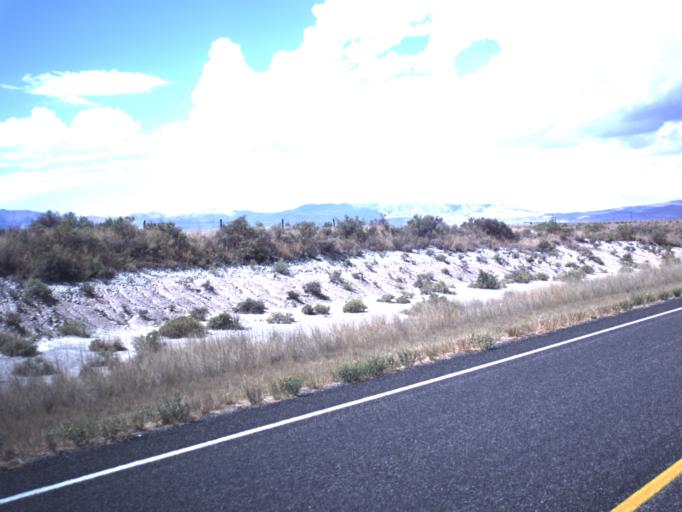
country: US
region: Utah
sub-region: Box Elder County
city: Tremonton
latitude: 41.5848
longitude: -112.2627
